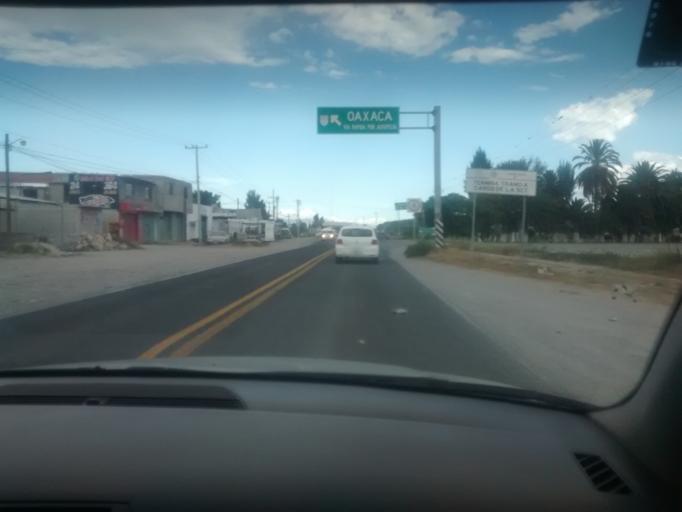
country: MX
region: Puebla
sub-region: Santiago Miahuatlan
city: San Jose Monte Chiquito
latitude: 18.4895
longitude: -97.4600
